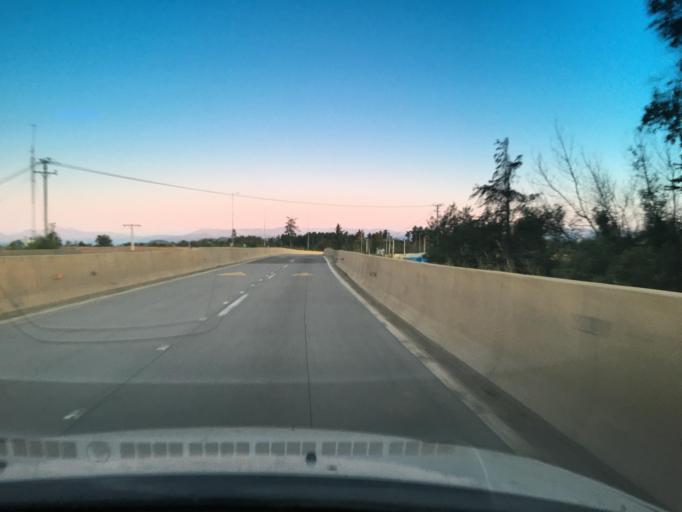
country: CL
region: Valparaiso
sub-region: Provincia de Valparaiso
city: Valparaiso
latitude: -33.0961
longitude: -71.5851
